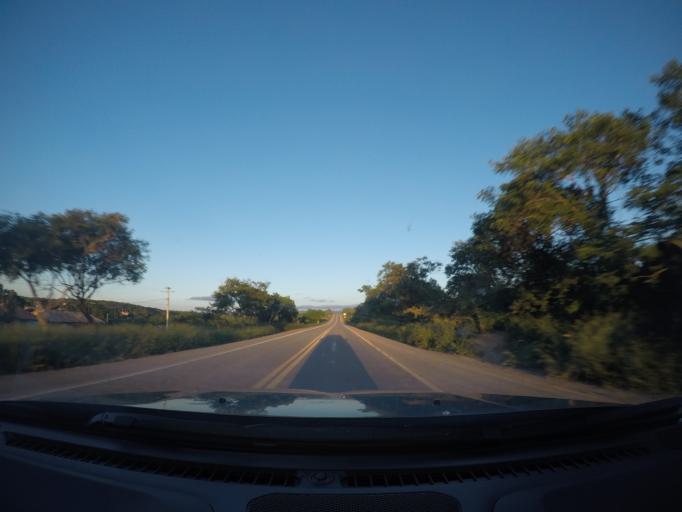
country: BR
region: Bahia
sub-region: Seabra
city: Seabra
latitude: -12.3966
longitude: -41.9338
